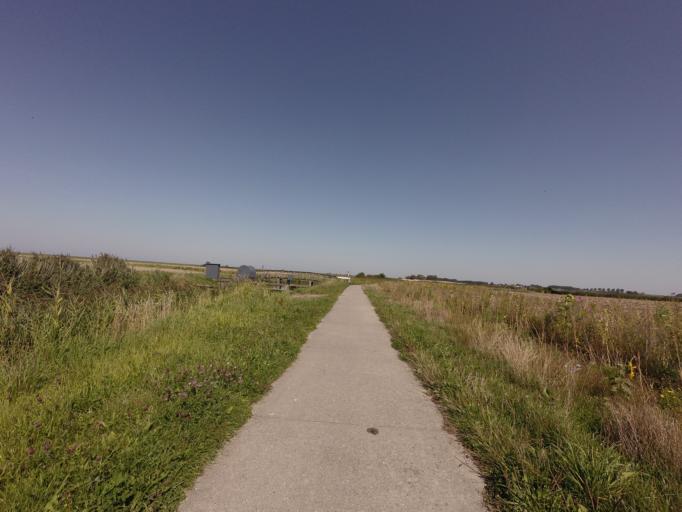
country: NL
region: Friesland
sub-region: Gemeente Dongeradeel
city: Anjum
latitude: 53.3915
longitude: 6.0667
